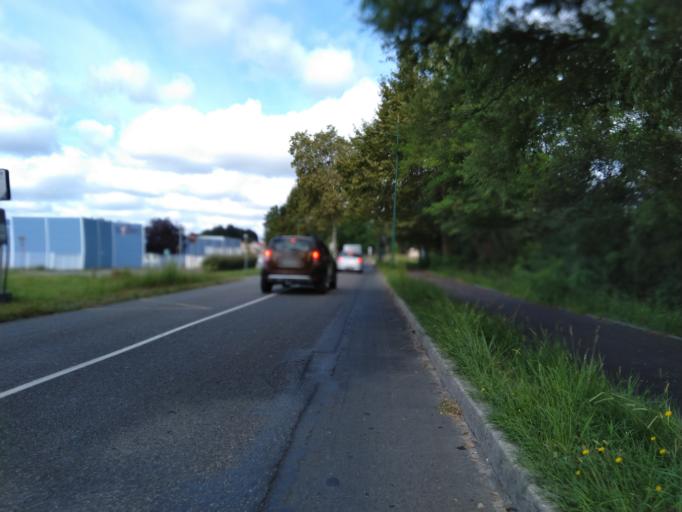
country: FR
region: Aquitaine
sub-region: Departement des Landes
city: Mees
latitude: 43.7292
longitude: -1.0896
